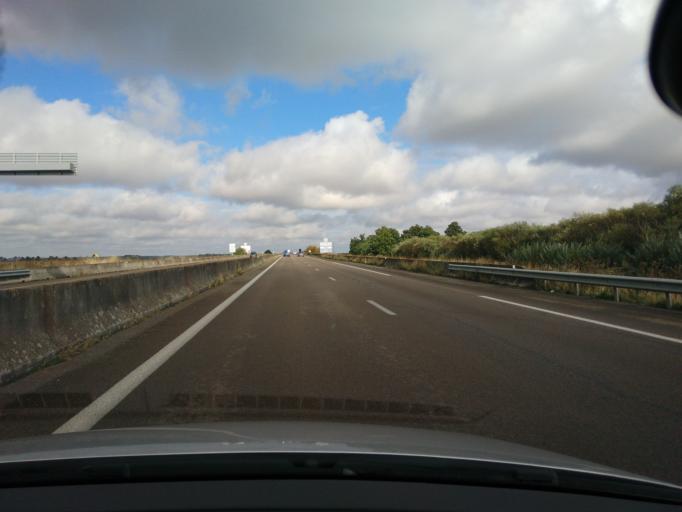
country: FR
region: Haute-Normandie
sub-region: Departement de l'Eure
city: La Madeleine-de-Nonancourt
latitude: 48.8568
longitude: 1.1789
